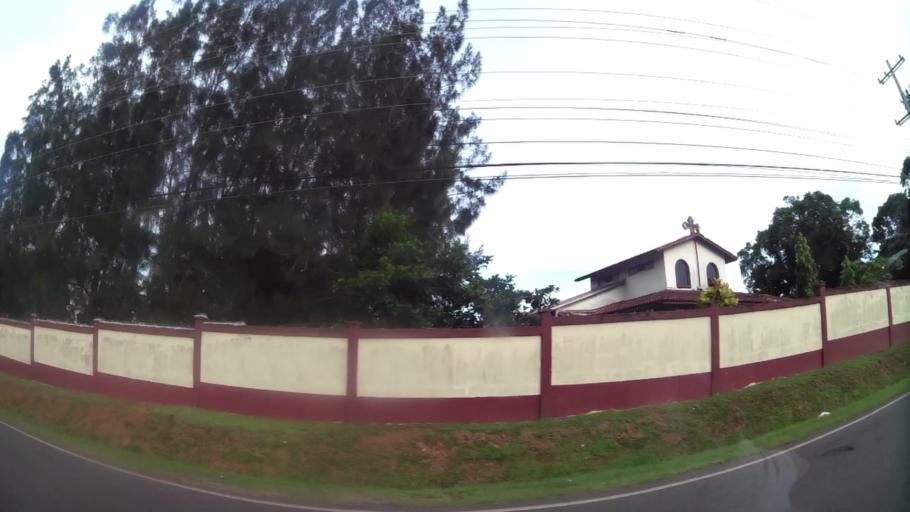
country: PA
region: Panama
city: La Chorrera
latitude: 8.8907
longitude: -79.7785
